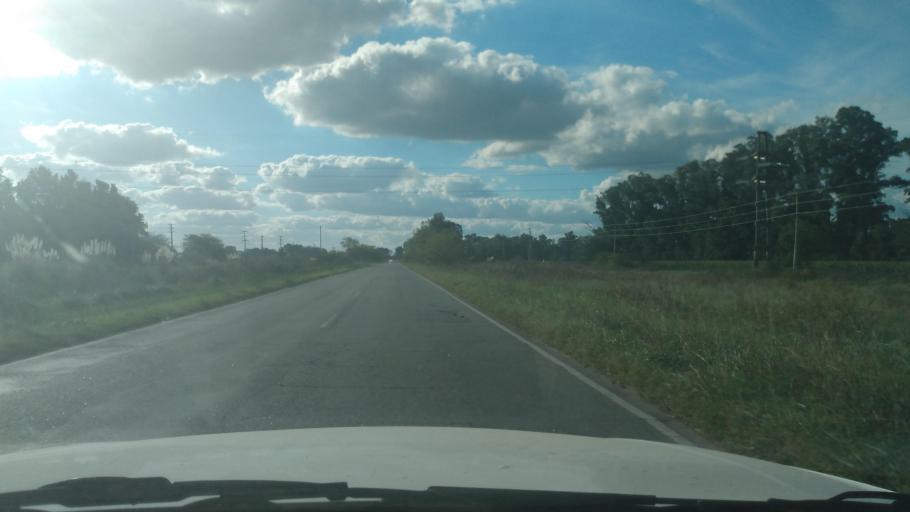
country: AR
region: Buenos Aires
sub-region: Partido de Mercedes
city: Mercedes
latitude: -34.7222
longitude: -59.3940
